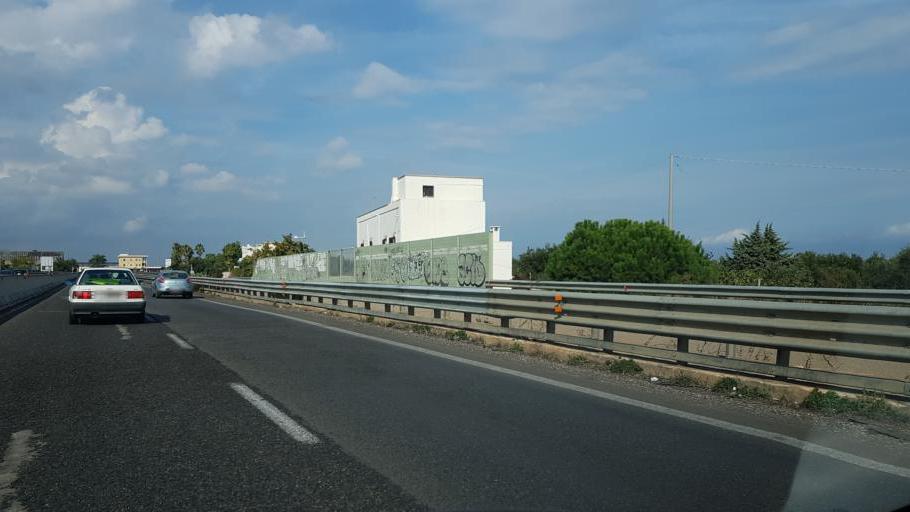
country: IT
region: Apulia
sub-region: Provincia di Brindisi
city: Fasano
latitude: 40.8555
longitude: 17.3525
